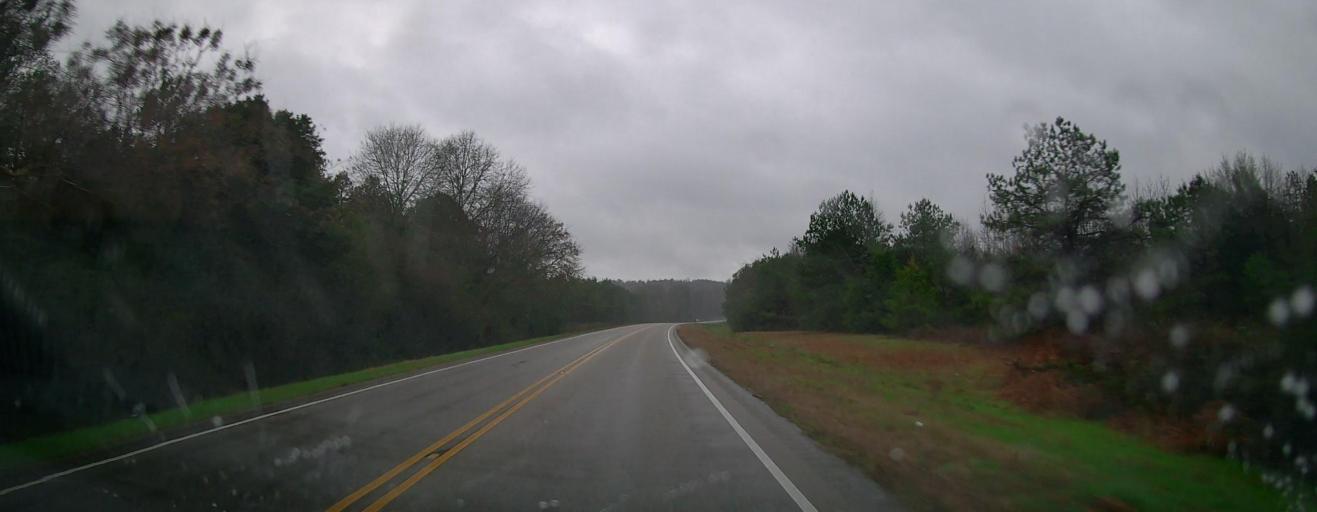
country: US
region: Alabama
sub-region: Autauga County
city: Prattville
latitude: 32.4930
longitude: -86.5757
